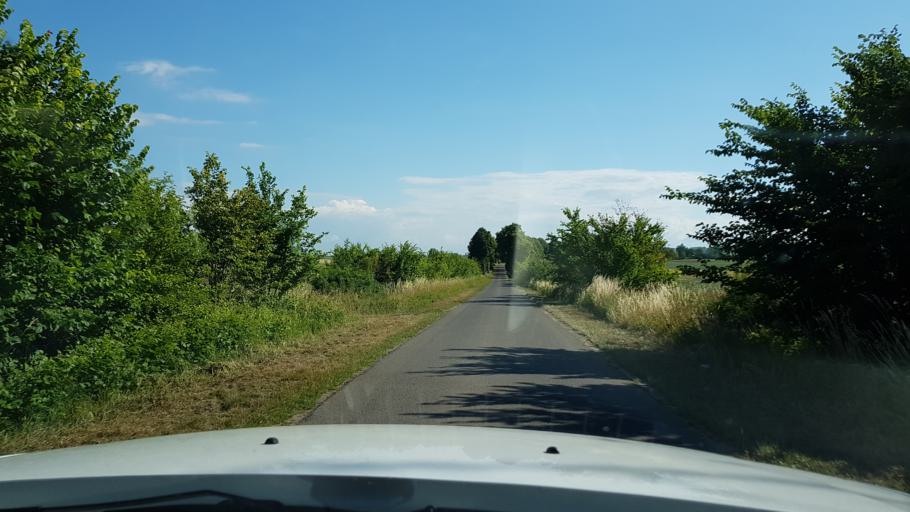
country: PL
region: West Pomeranian Voivodeship
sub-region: Powiat gryficki
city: Mrzezyno
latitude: 54.1015
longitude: 15.3040
